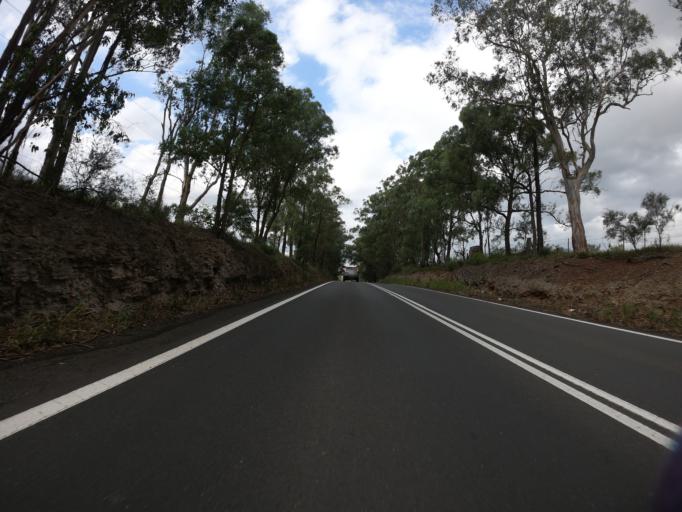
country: AU
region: New South Wales
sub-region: Blacktown
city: Riverstone
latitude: -33.6642
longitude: 150.8904
